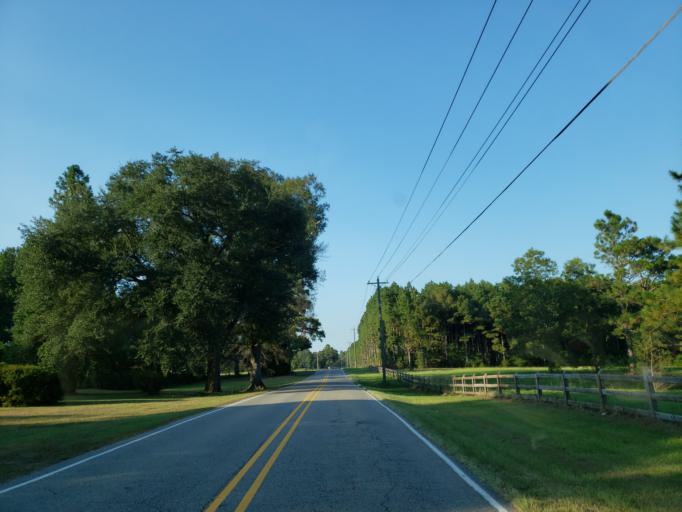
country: US
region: Mississippi
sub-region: Lamar County
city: West Hattiesburg
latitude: 31.3043
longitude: -89.4450
